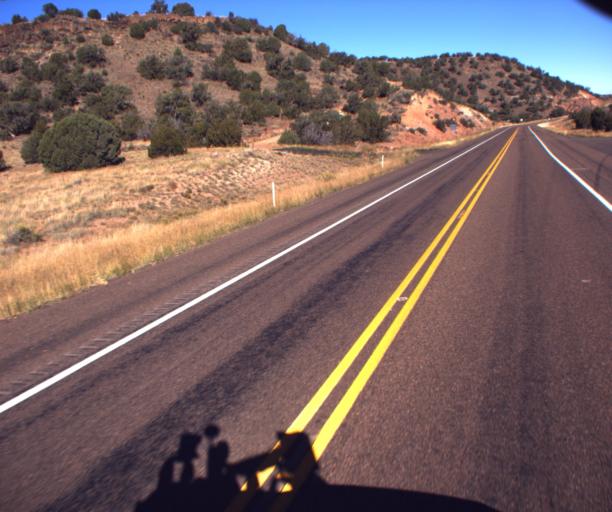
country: US
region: Arizona
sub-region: Navajo County
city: White Mountain Lake
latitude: 34.3872
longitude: -110.0622
